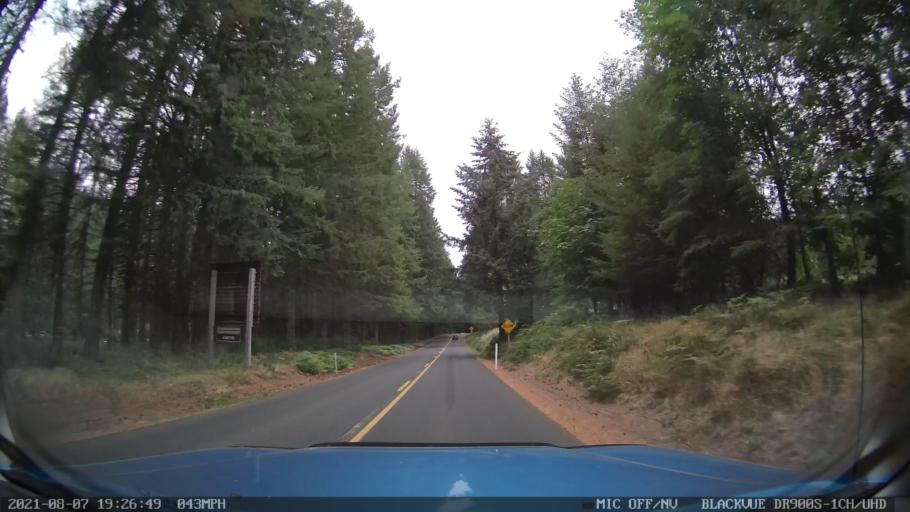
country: US
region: Oregon
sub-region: Linn County
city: Lyons
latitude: 44.8757
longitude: -122.6515
